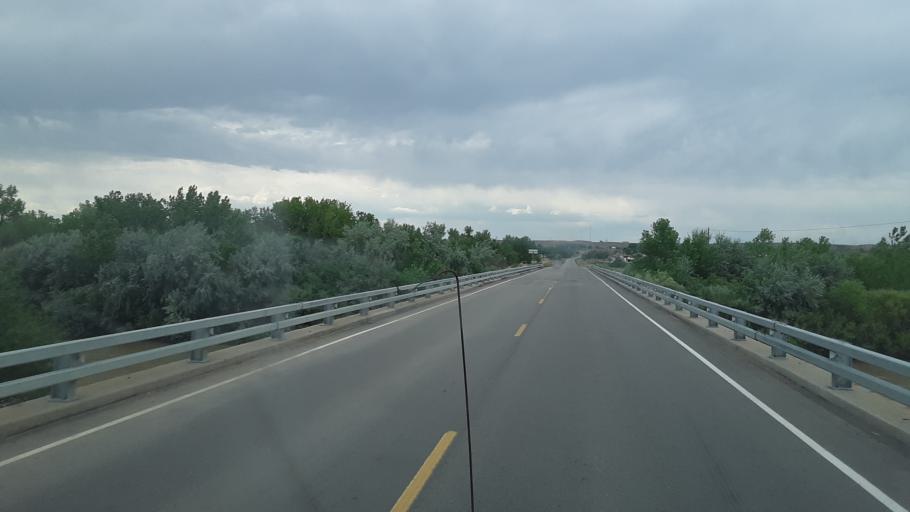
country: US
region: Colorado
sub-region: Otero County
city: Fowler
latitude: 38.1407
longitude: -104.0227
